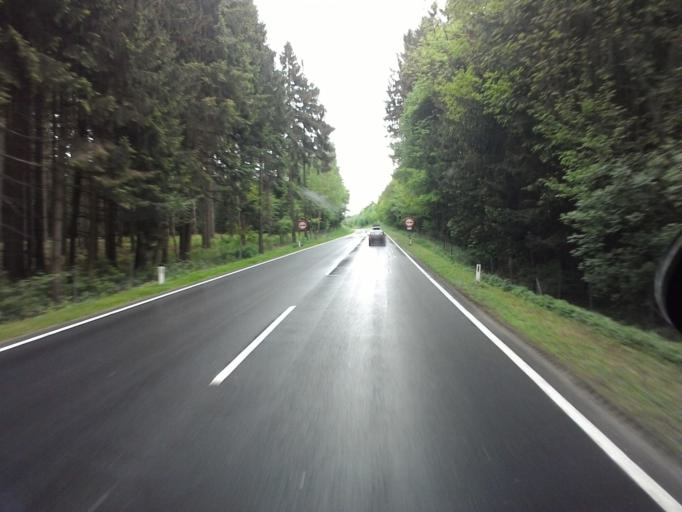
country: AT
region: Upper Austria
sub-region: Wels-Land
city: Steinhaus
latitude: 48.0960
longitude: 14.0411
